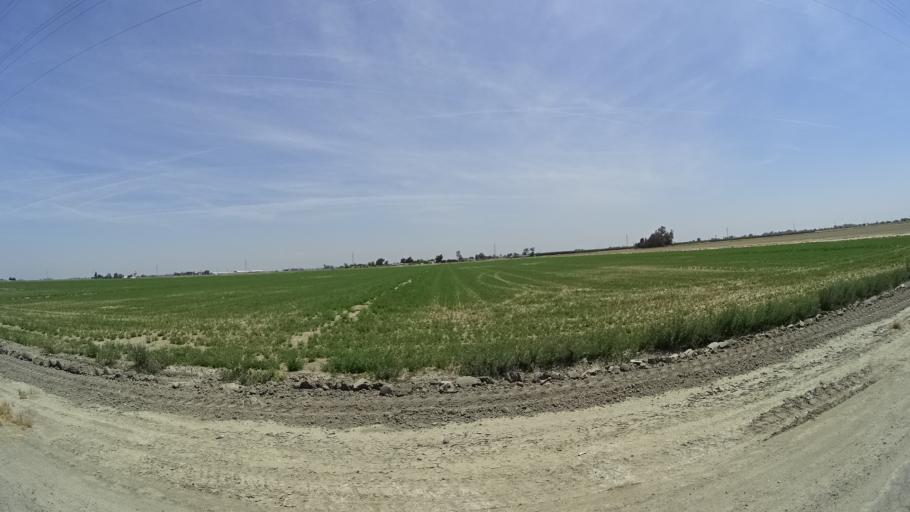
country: US
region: California
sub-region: Fresno County
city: Riverdale
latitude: 36.3962
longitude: -119.9051
